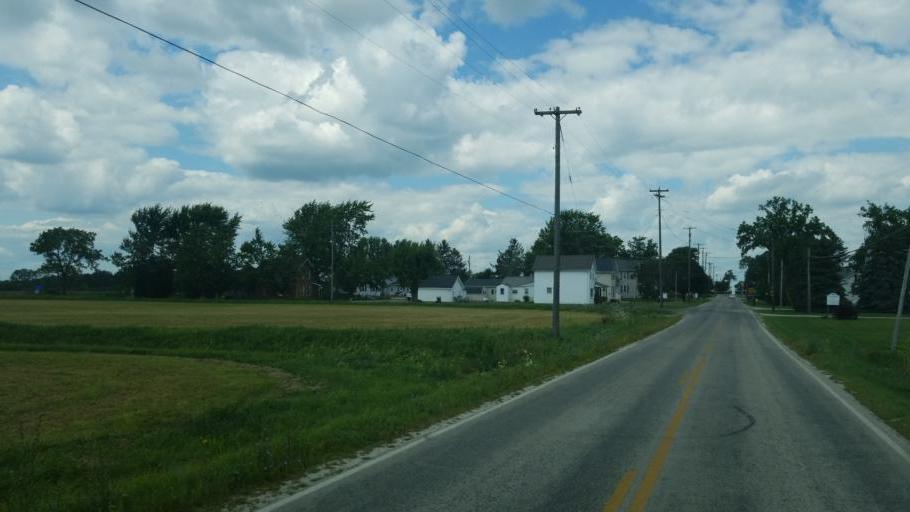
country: US
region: Ohio
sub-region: Ottawa County
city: Elmore
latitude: 41.5447
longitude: -83.2802
